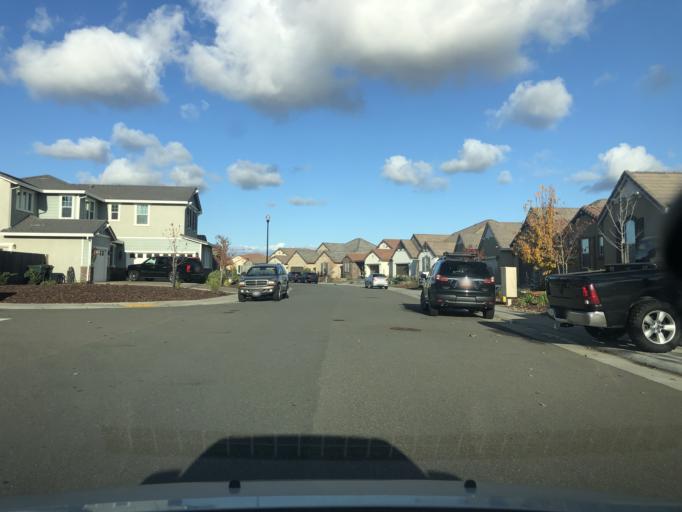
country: US
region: California
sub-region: Sacramento County
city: Antelope
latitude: 38.7737
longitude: -121.3808
